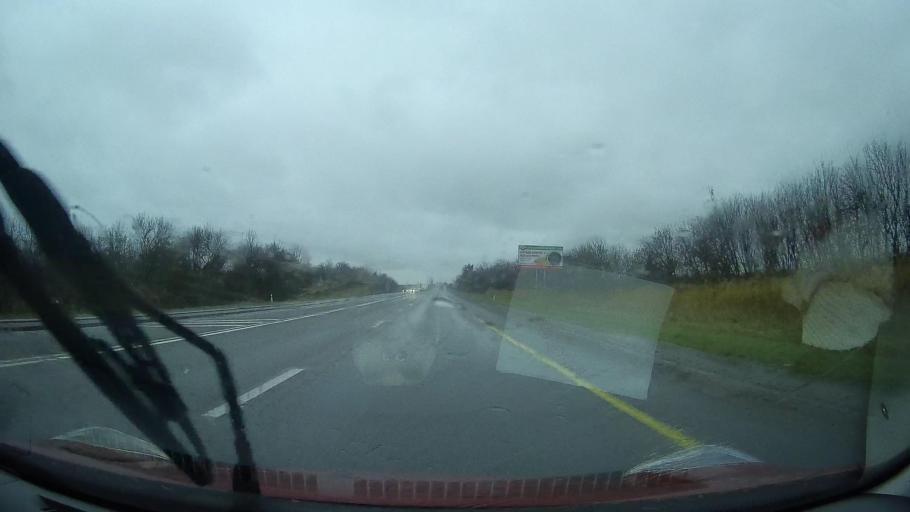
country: RU
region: Stavropol'skiy
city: Nevinnomyssk
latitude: 44.6347
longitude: 42.0038
